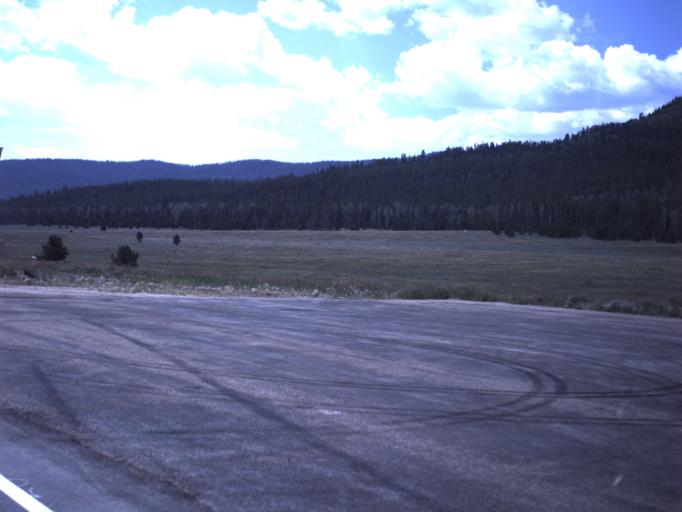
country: US
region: Utah
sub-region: Daggett County
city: Manila
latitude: 40.7830
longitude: -109.4709
